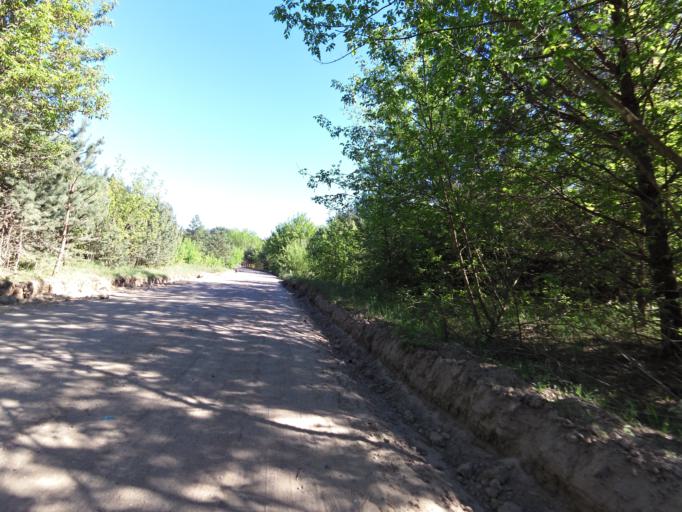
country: LT
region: Vilnius County
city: Pilaite
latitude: 54.6783
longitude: 25.1633
